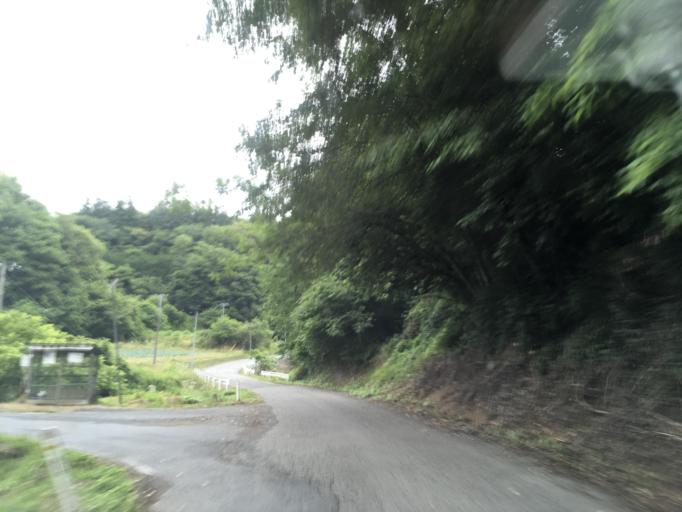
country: JP
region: Iwate
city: Ichinoseki
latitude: 38.8509
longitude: 141.3207
